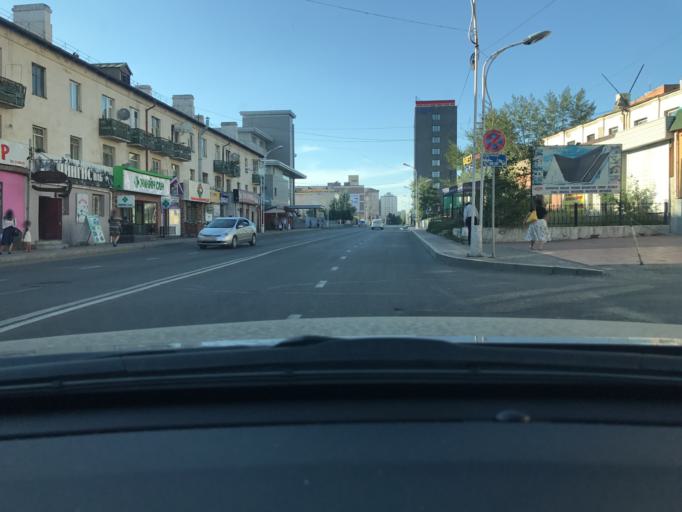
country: MN
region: Ulaanbaatar
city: Ulaanbaatar
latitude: 47.9190
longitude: 106.9353
